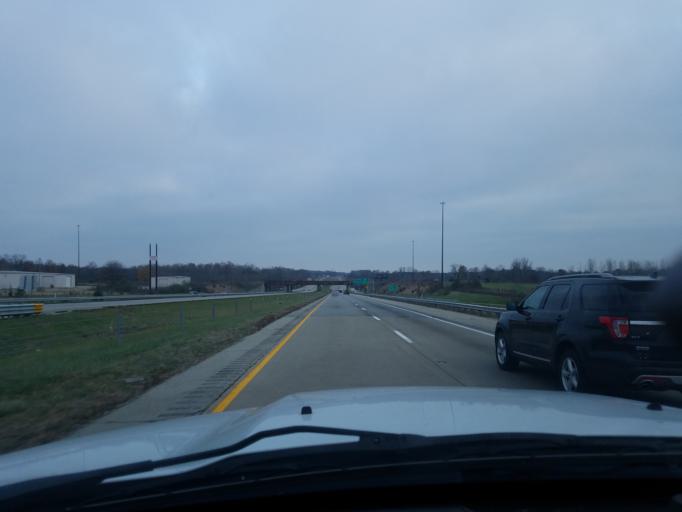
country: US
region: Indiana
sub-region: Delaware County
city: Daleville
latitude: 40.1148
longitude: -85.5687
